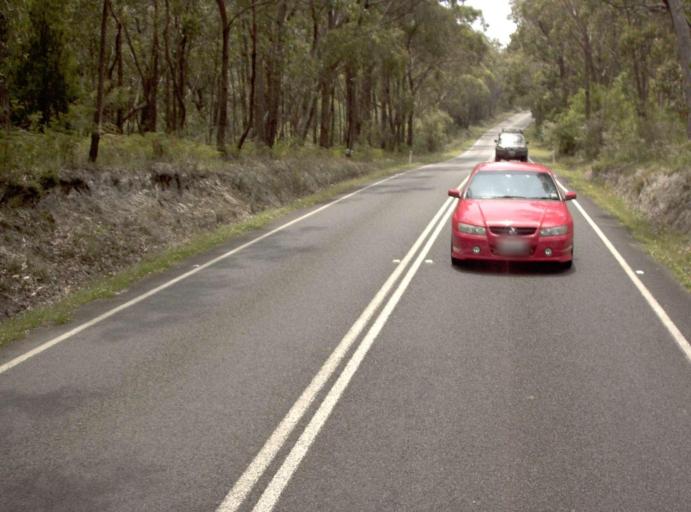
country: AU
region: Victoria
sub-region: Latrobe
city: Traralgon
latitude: -38.4134
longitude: 146.7489
